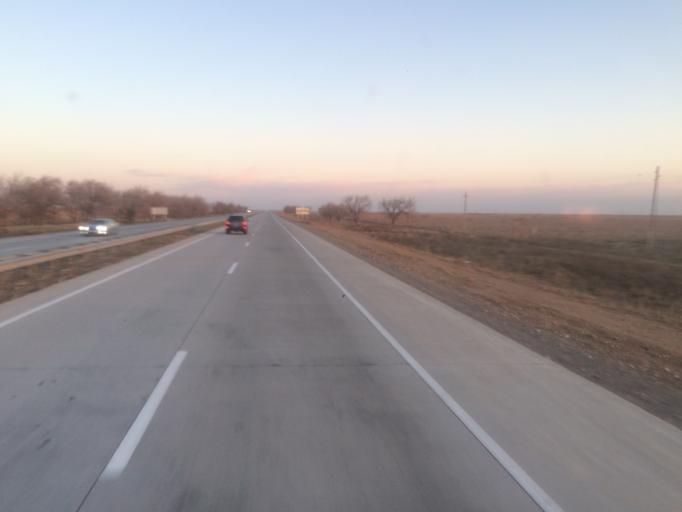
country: KZ
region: Ongtustik Qazaqstan
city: Bayaldyr
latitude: 43.0582
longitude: 68.6875
